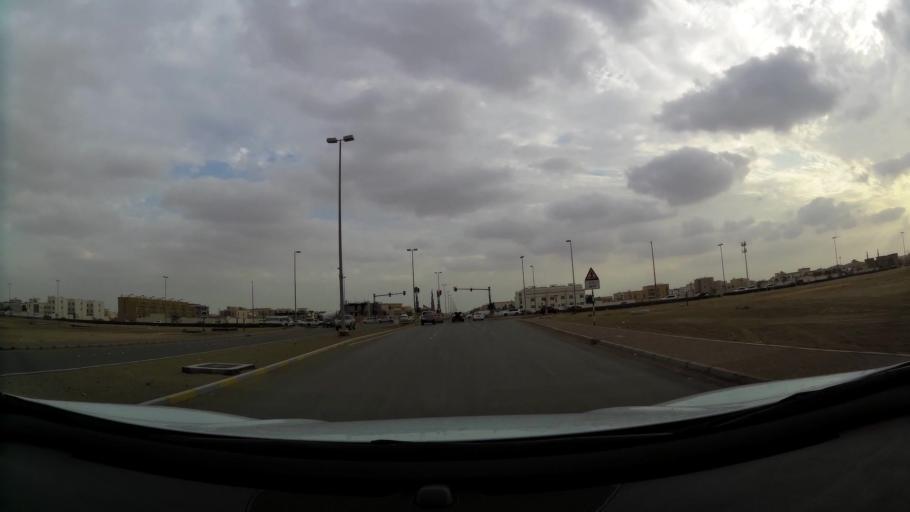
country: AE
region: Abu Dhabi
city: Abu Dhabi
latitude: 24.3487
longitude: 54.5530
